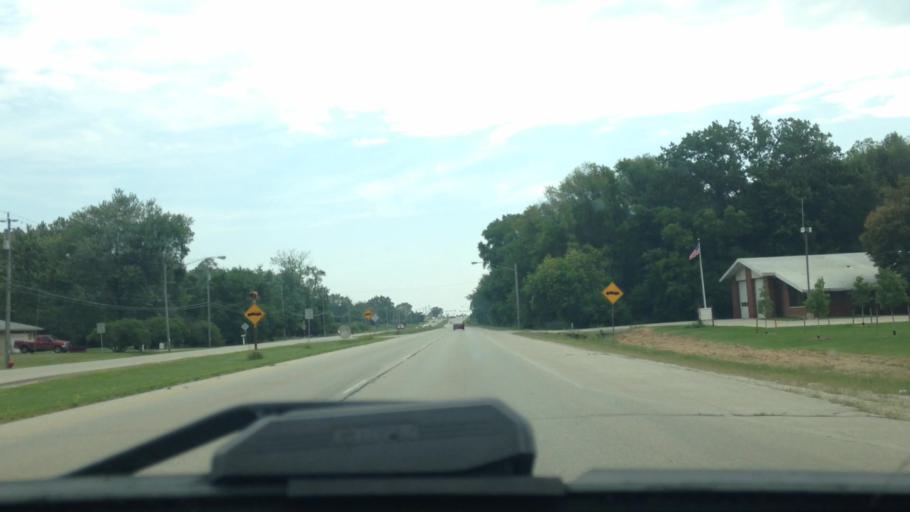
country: US
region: Wisconsin
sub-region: Waukesha County
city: Butler
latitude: 43.1191
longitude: -88.0989
